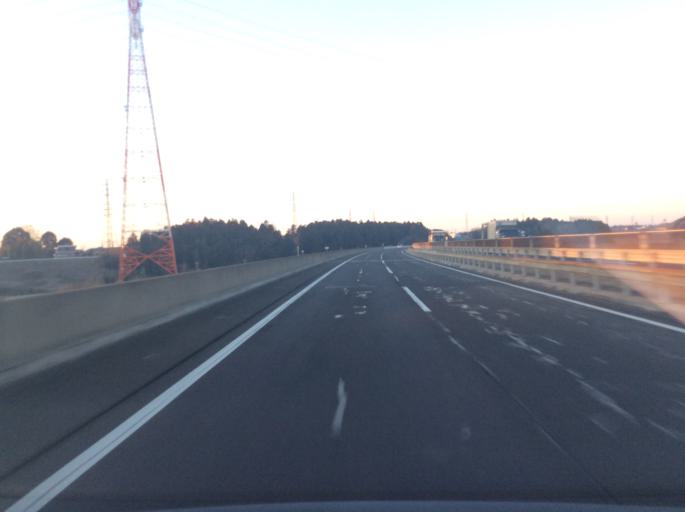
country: JP
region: Ibaraki
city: Funaishikawa
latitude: 36.4943
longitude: 140.5640
